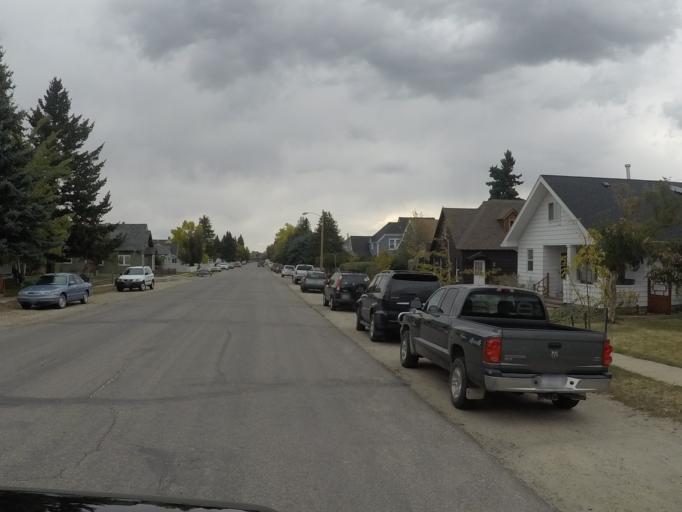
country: US
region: Montana
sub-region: Carbon County
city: Red Lodge
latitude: 45.1873
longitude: -109.2457
